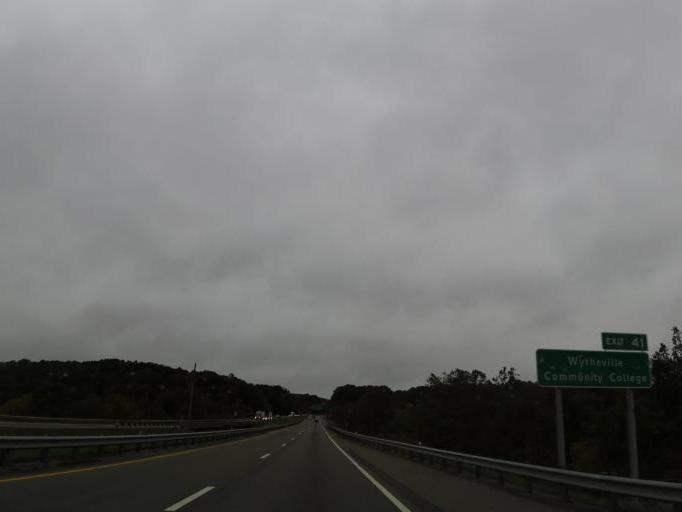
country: US
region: Virginia
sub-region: Wythe County
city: Wytheville
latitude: 36.9832
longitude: -81.0729
